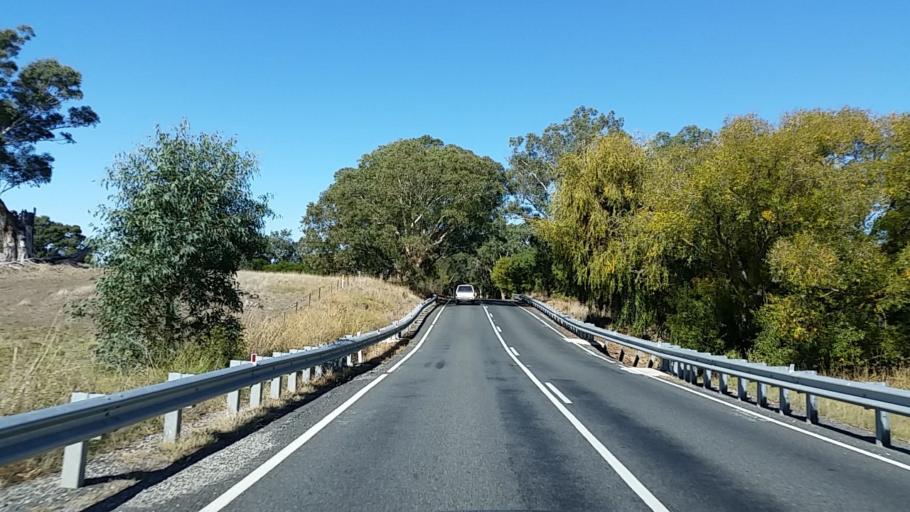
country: AU
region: South Australia
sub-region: Adelaide Hills
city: Birdwood
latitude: -34.7654
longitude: 139.0177
